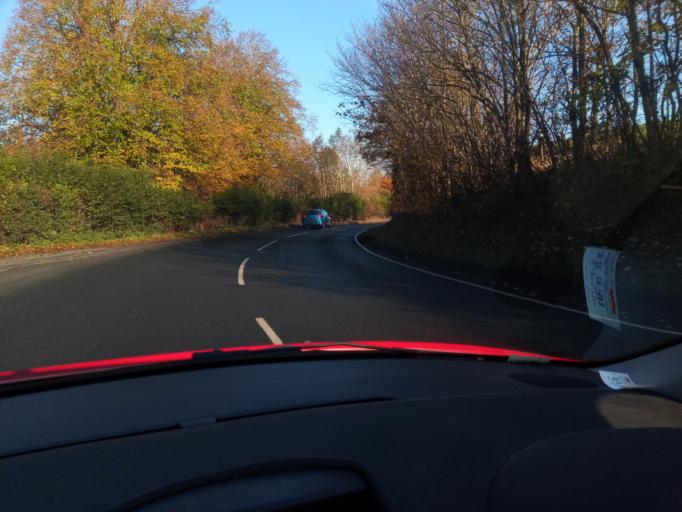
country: GB
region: Scotland
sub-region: The Scottish Borders
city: Hawick
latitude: 55.4376
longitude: -2.7485
